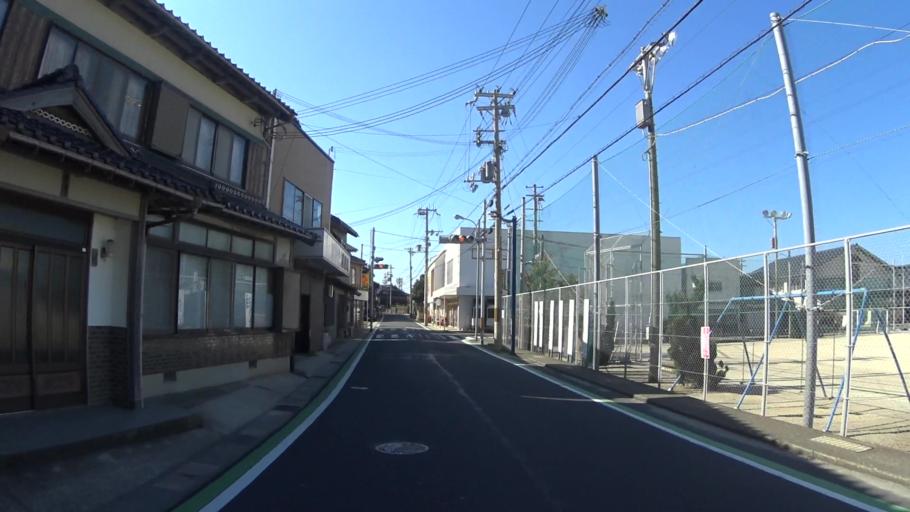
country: JP
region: Kyoto
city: Miyazu
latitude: 35.7375
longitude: 135.0892
